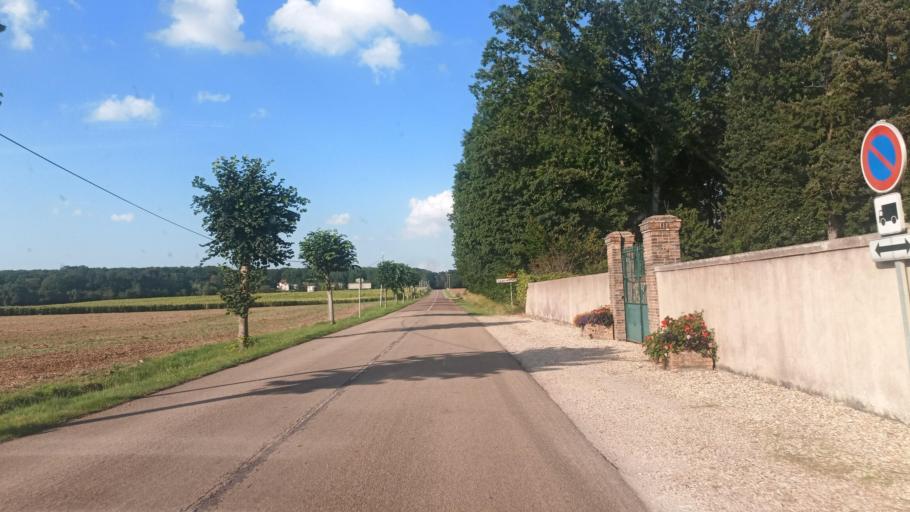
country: FR
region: Bourgogne
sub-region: Departement de l'Yonne
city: Pont-sur-Yonne
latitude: 48.2493
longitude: 3.1612
